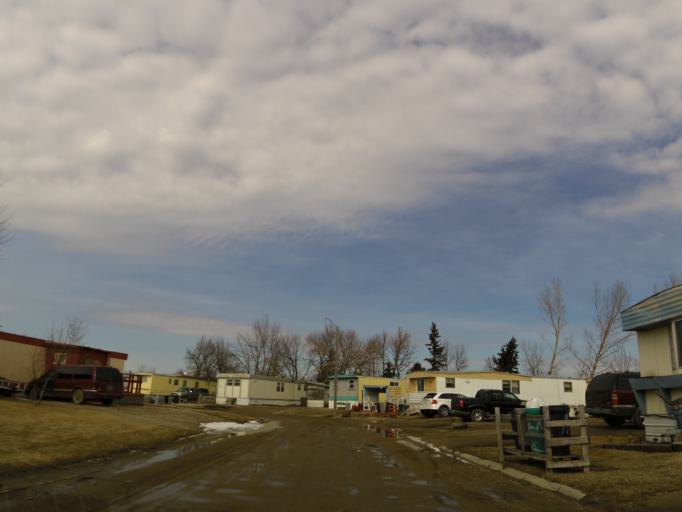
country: US
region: North Dakota
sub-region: Walsh County
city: Grafton
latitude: 48.2948
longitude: -97.3800
